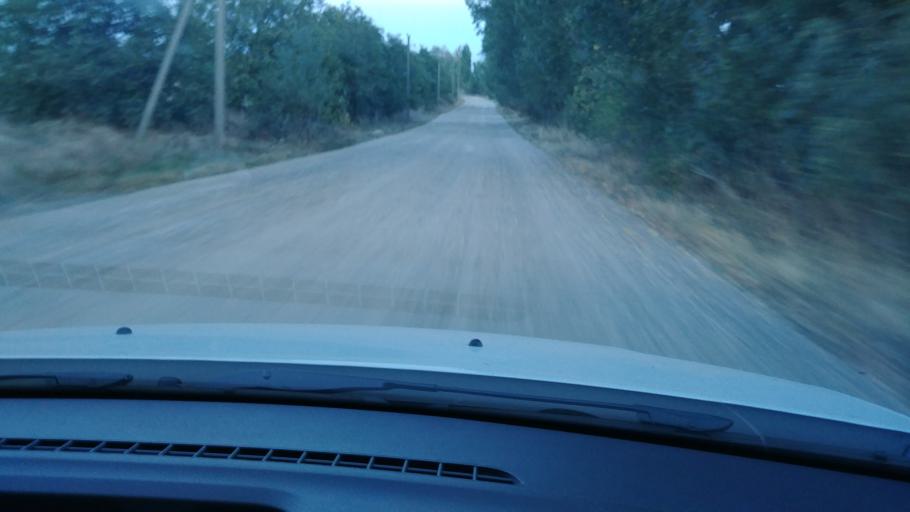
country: MD
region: Rezina
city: Saharna
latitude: 47.6777
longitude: 28.9242
